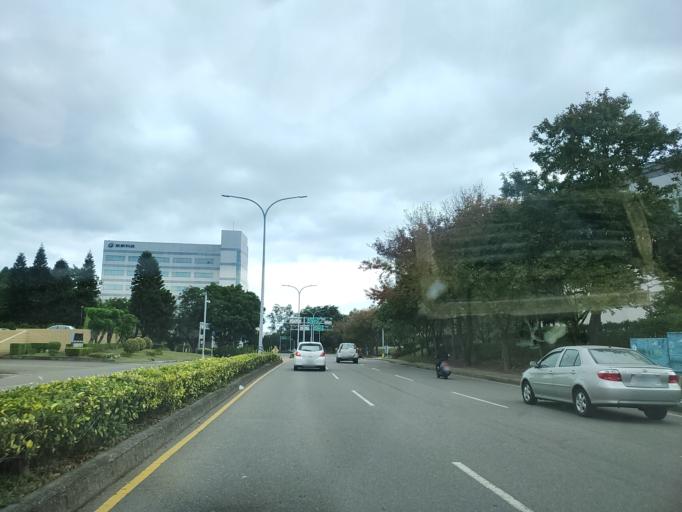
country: TW
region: Taiwan
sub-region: Hsinchu
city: Hsinchu
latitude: 24.7765
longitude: 121.0061
